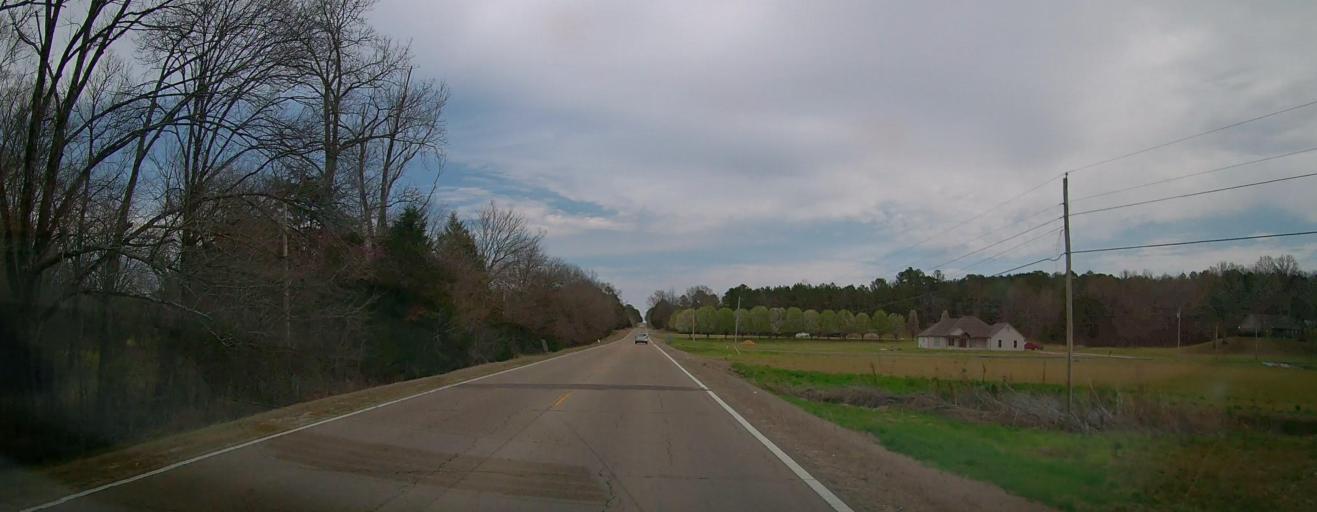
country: US
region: Mississippi
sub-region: Lee County
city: Plantersville
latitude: 34.2661
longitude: -88.6058
